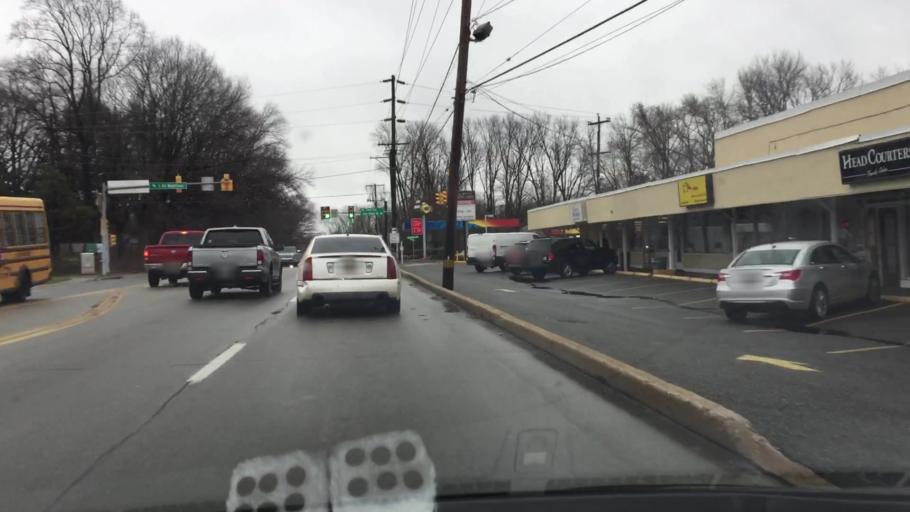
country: US
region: Pennsylvania
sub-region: Delaware County
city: Lima
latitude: 39.9051
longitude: -75.4154
